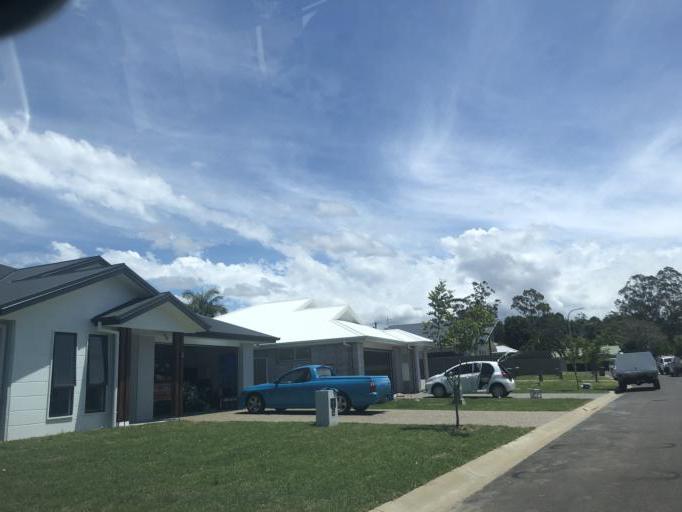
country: AU
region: New South Wales
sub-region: Coffs Harbour
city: Coffs Harbour
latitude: -30.2891
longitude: 153.0937
